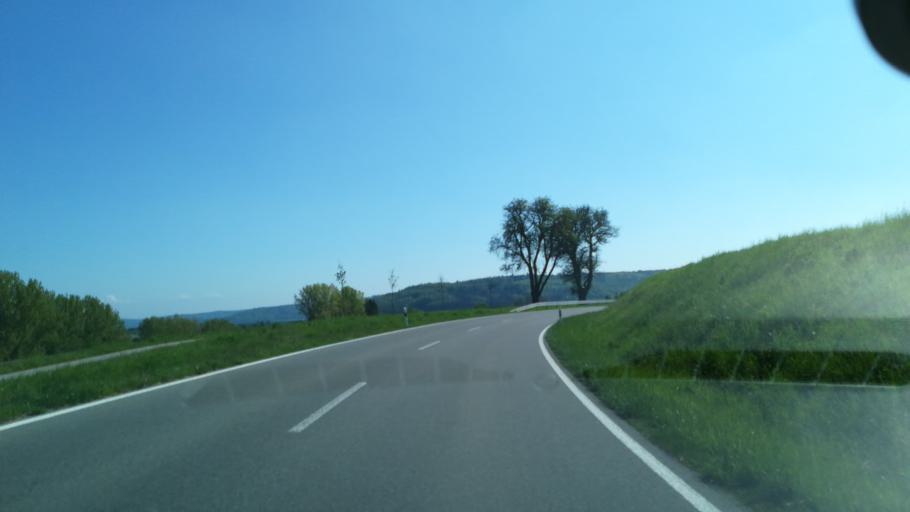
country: DE
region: Baden-Wuerttemberg
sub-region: Freiburg Region
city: Hilzingen
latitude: 47.7728
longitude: 8.7898
